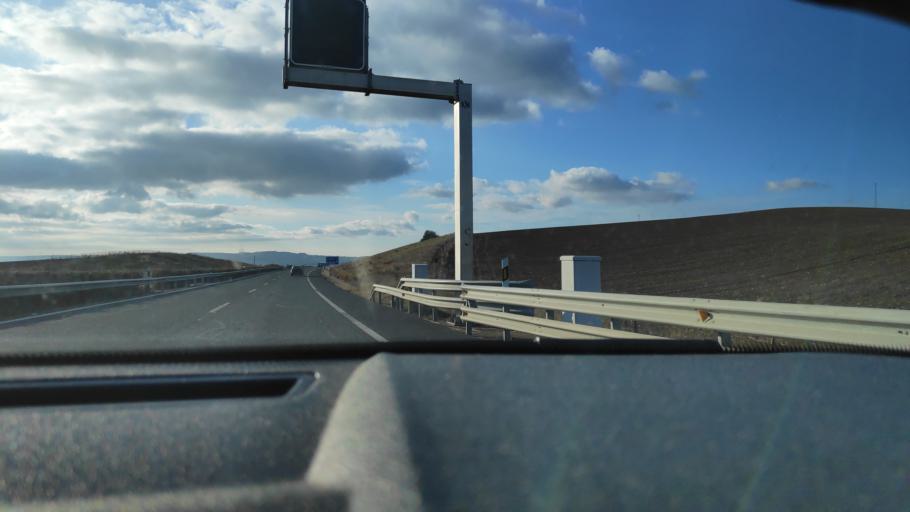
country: ES
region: Andalusia
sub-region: Provincia de Sevilla
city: Carmona
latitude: 37.4842
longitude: -5.5243
